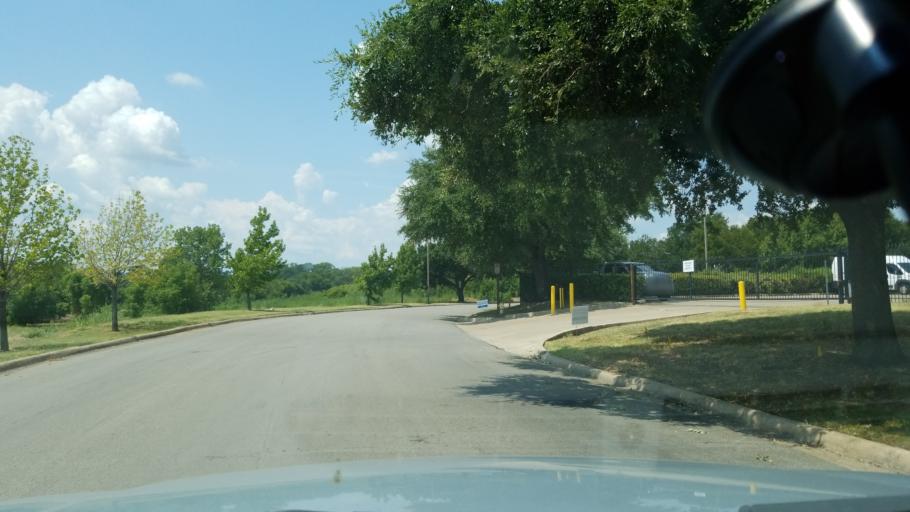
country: US
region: Texas
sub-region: Dallas County
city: Irving
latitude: 32.8563
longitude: -96.8959
